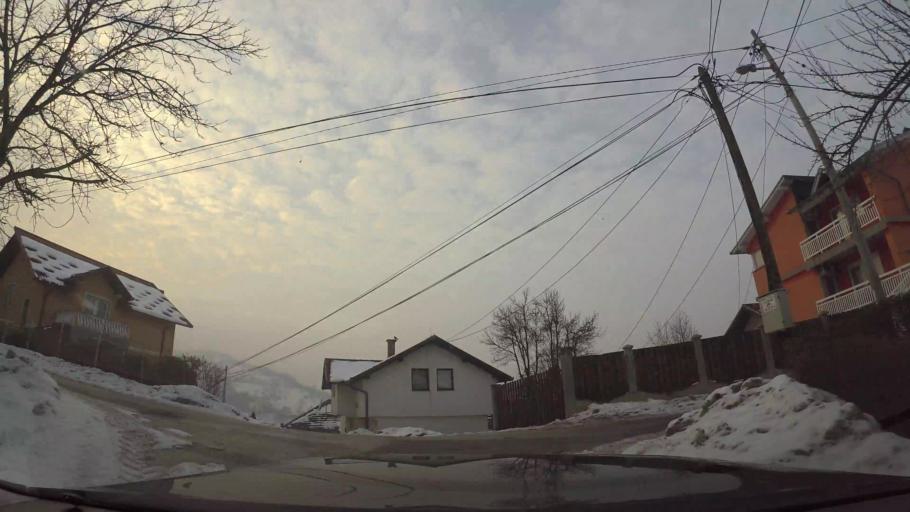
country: BA
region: Federation of Bosnia and Herzegovina
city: Hotonj
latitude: 43.8916
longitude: 18.3668
